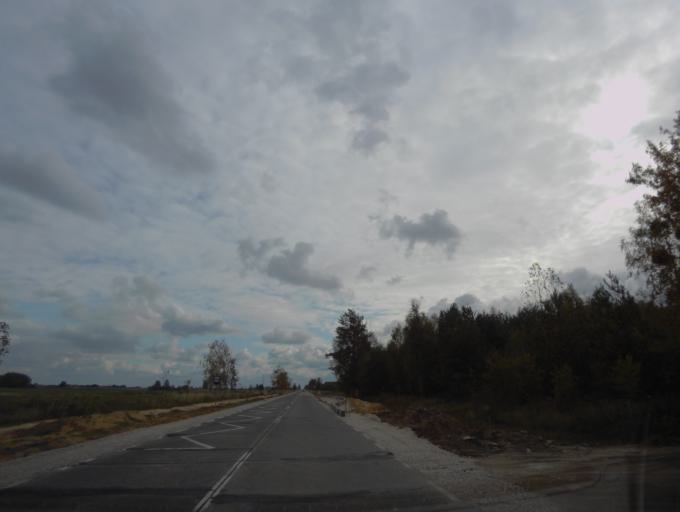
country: PL
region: Lublin Voivodeship
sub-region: Powiat wlodawski
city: Wlodawa
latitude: 51.5654
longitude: 23.5110
